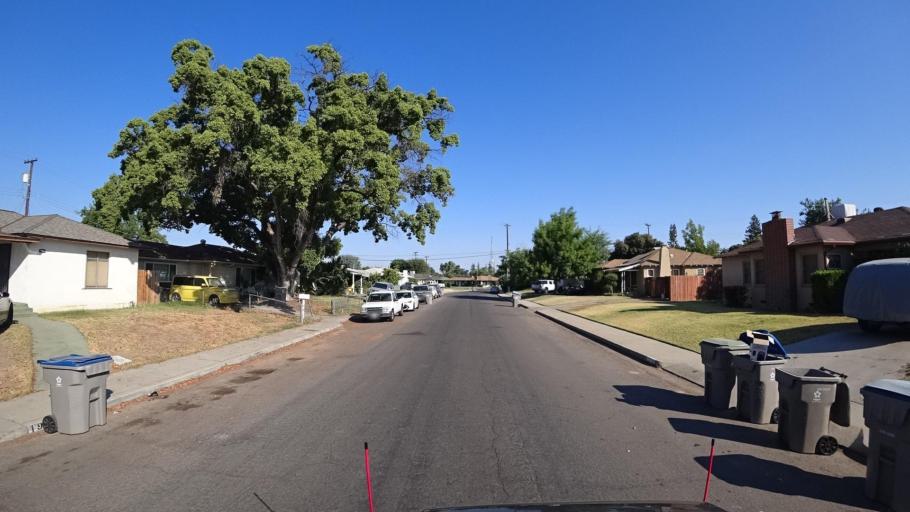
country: US
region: California
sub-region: Fresno County
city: Fresno
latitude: 36.7679
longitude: -119.7695
